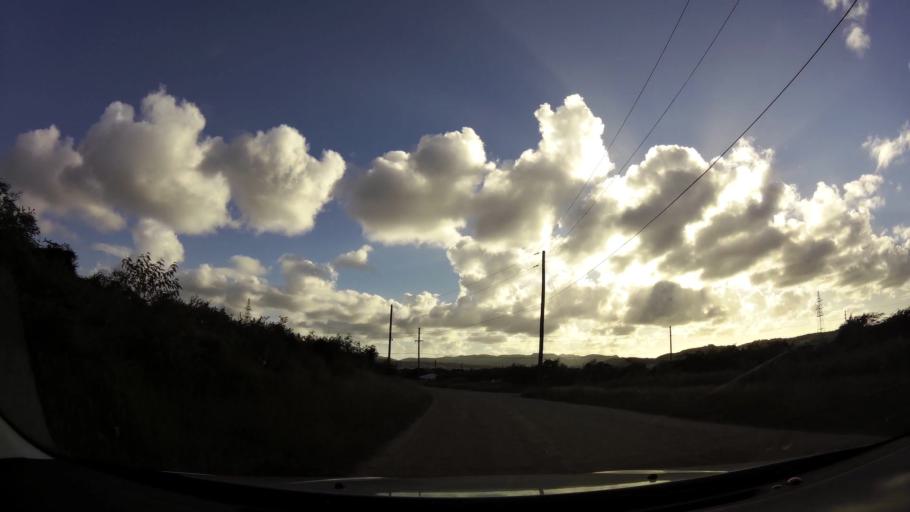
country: AG
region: Saint George
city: Piggotts
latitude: 17.1173
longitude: -61.7947
